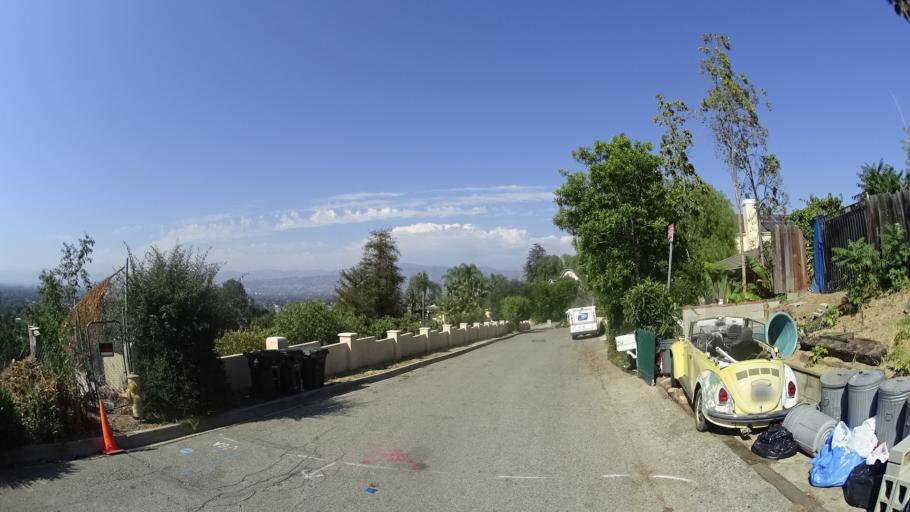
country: US
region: California
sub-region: Los Angeles County
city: Universal City
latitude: 34.1380
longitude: -118.3736
